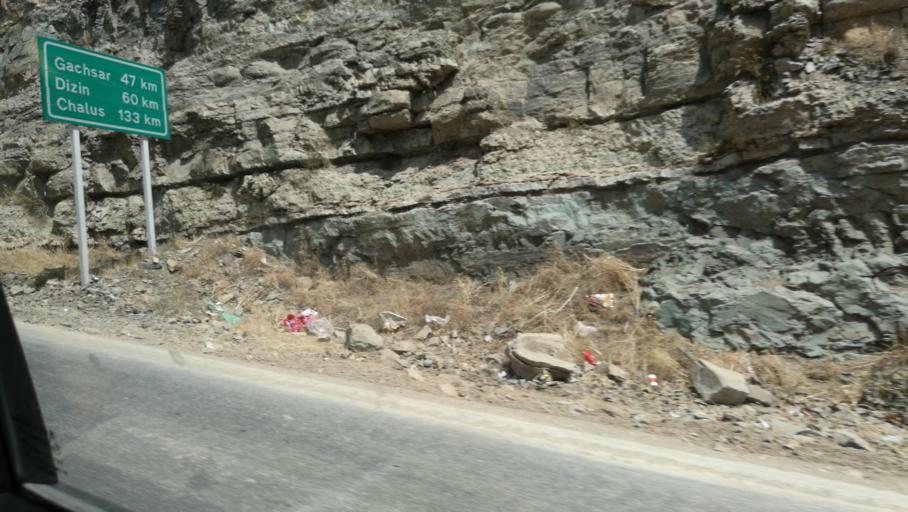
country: IR
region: Alborz
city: Karaj
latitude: 35.9415
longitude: 51.0770
